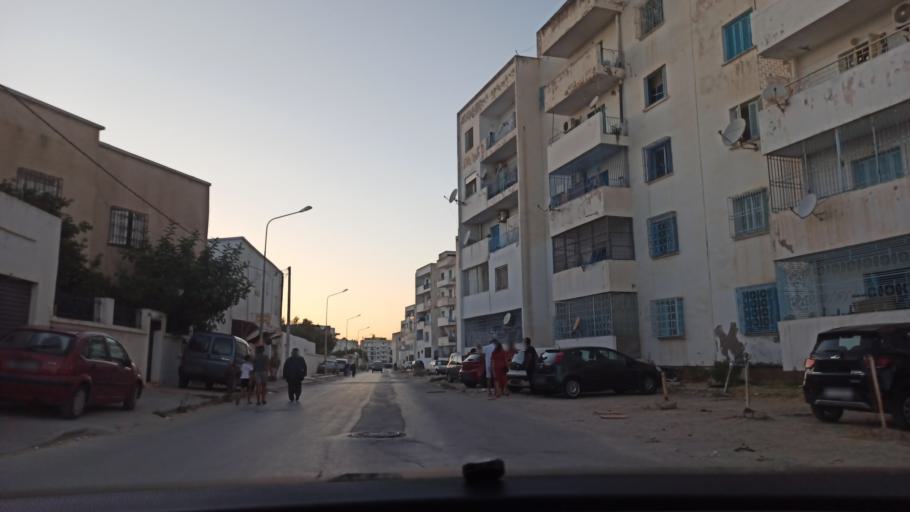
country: TN
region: Ariana
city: Ariana
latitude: 36.8657
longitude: 10.1977
